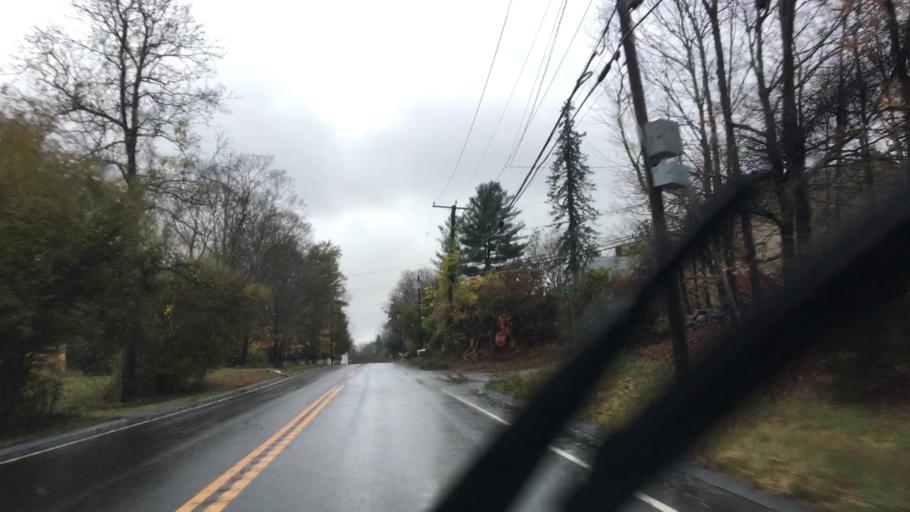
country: US
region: Connecticut
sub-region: New Haven County
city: Oxford
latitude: 41.4297
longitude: -73.1568
